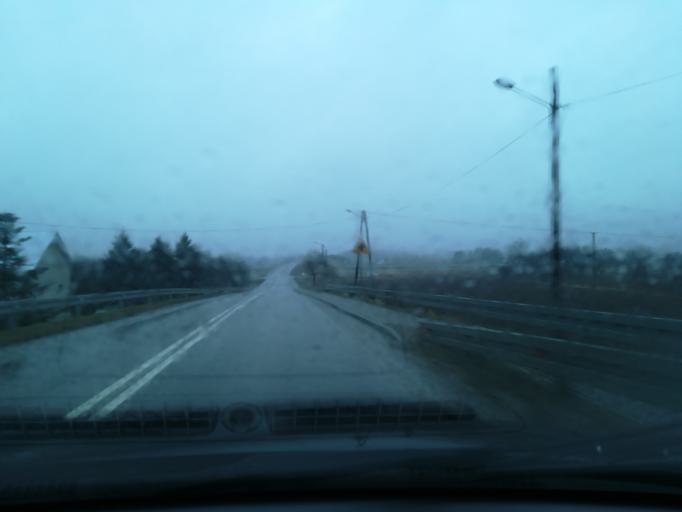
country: PL
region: Subcarpathian Voivodeship
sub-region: Powiat lancucki
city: Bialobrzegi
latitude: 50.1123
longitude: 22.3361
